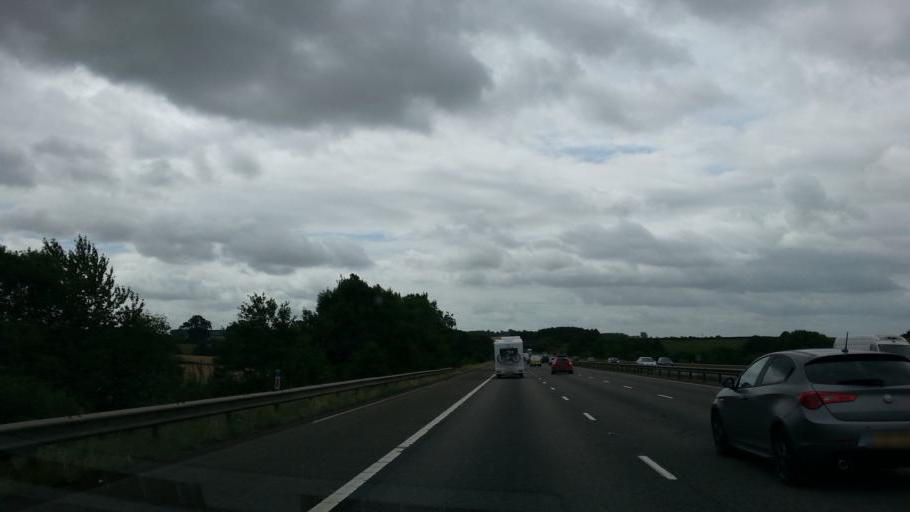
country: GB
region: England
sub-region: Oxfordshire
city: Somerton
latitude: 51.9856
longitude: -1.2659
